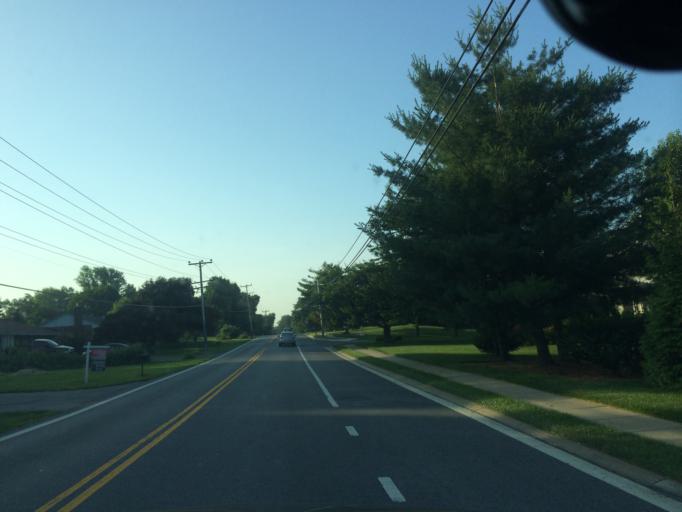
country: US
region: Maryland
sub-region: Carroll County
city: Eldersburg
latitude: 39.3863
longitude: -76.9233
